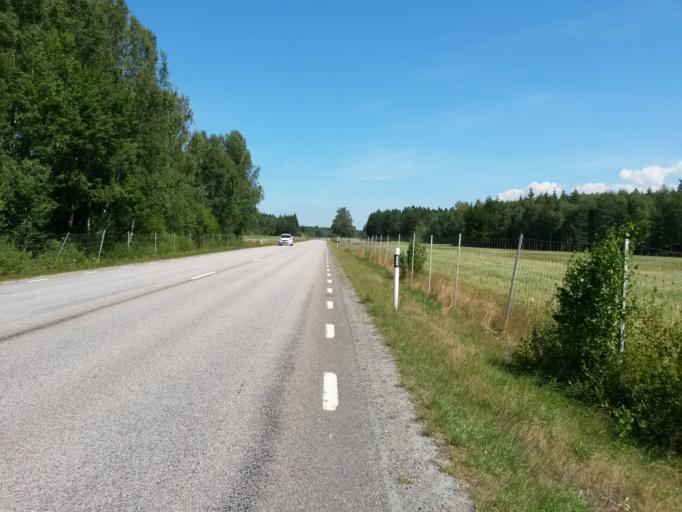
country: SE
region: Vaestra Goetaland
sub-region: Vara Kommun
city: Vara
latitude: 58.4444
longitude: 12.9668
